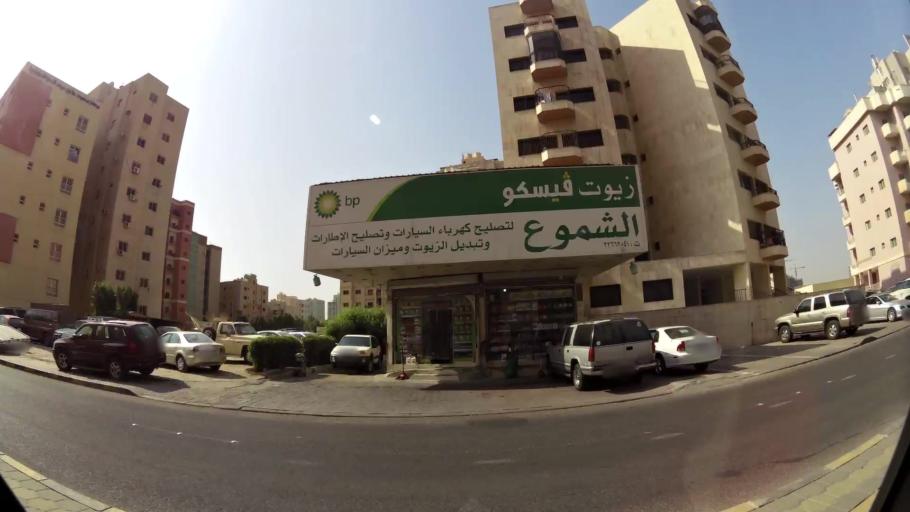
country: KW
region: Muhafazat Hawalli
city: Hawalli
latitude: 29.3383
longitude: 48.0282
